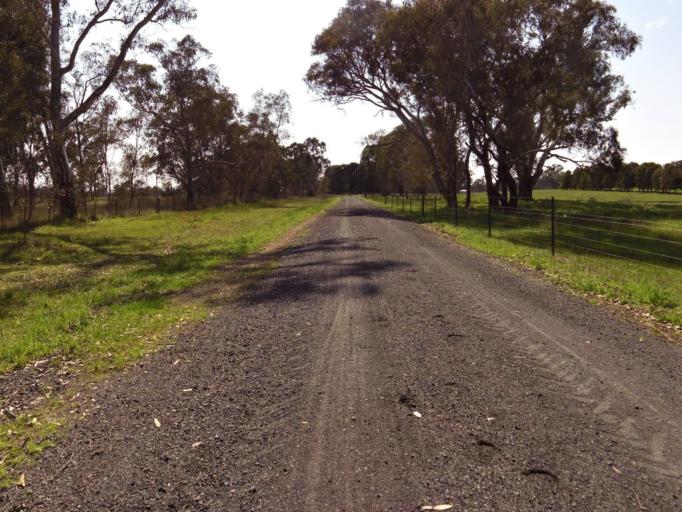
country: AU
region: Victoria
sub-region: Murrindindi
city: Alexandra
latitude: -37.1133
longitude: 145.6082
